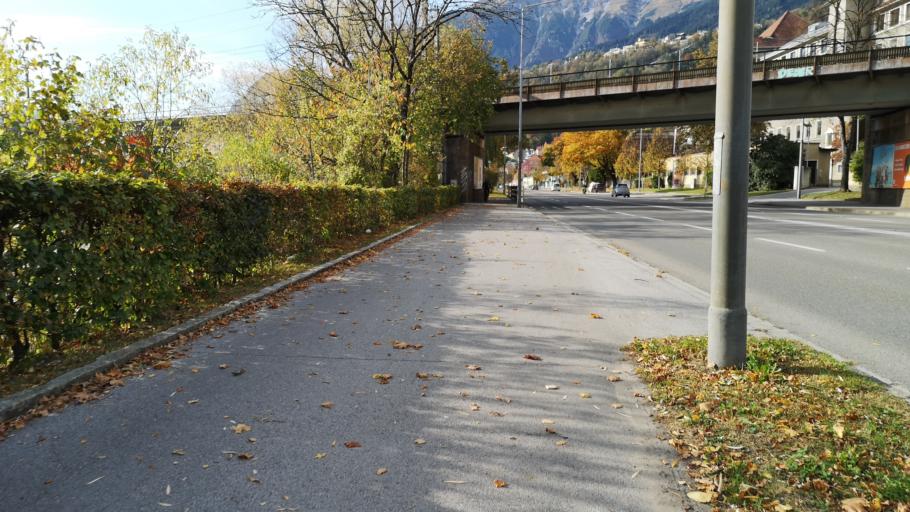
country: AT
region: Tyrol
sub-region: Innsbruck Stadt
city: Innsbruck
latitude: 47.2790
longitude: 11.4171
